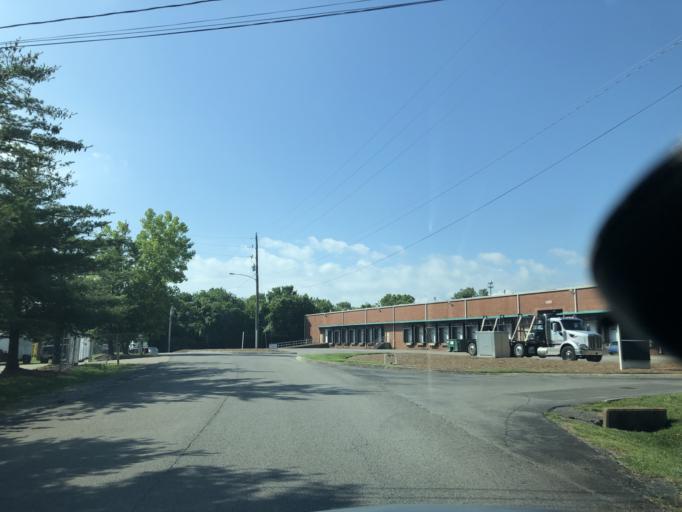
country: US
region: Tennessee
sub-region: Rutherford County
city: La Vergne
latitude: 36.0123
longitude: -86.6154
